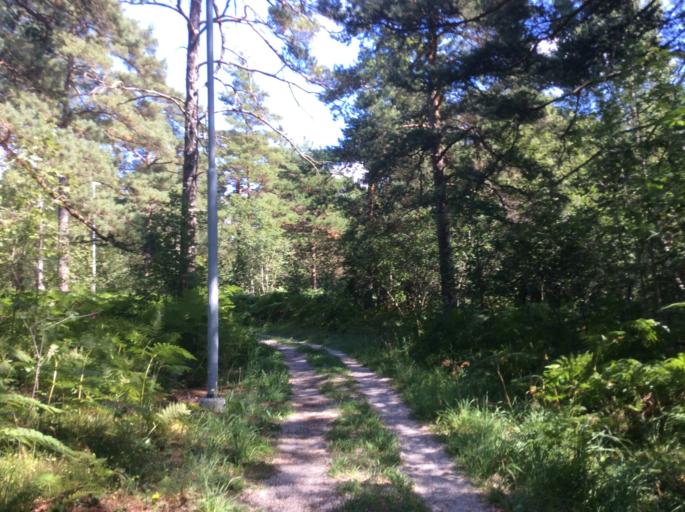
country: SE
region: Gotland
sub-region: Gotland
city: Vibble
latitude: 57.6002
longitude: 18.2765
